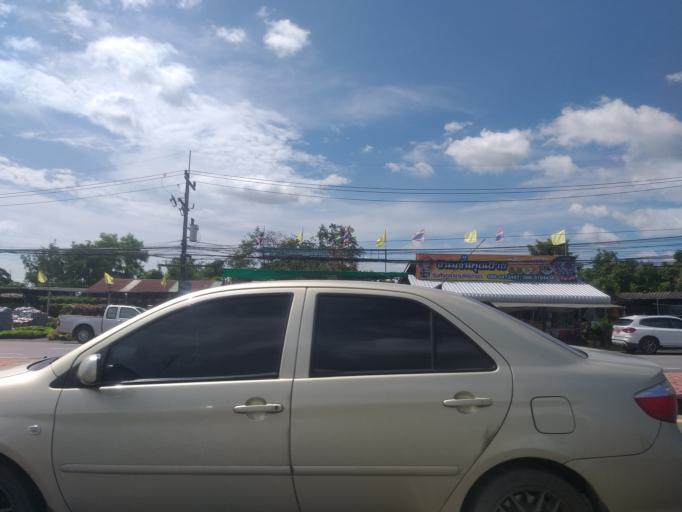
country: TH
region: Nakhon Nayok
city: Nakhon Nayok
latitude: 14.2197
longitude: 101.2282
